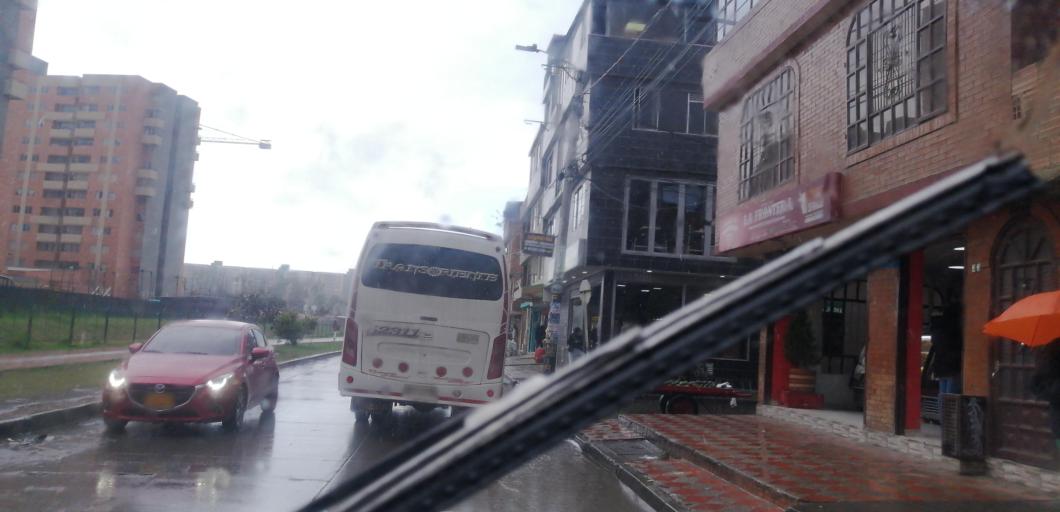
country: CO
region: Cundinamarca
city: Madrid
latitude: 4.7307
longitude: -74.2806
